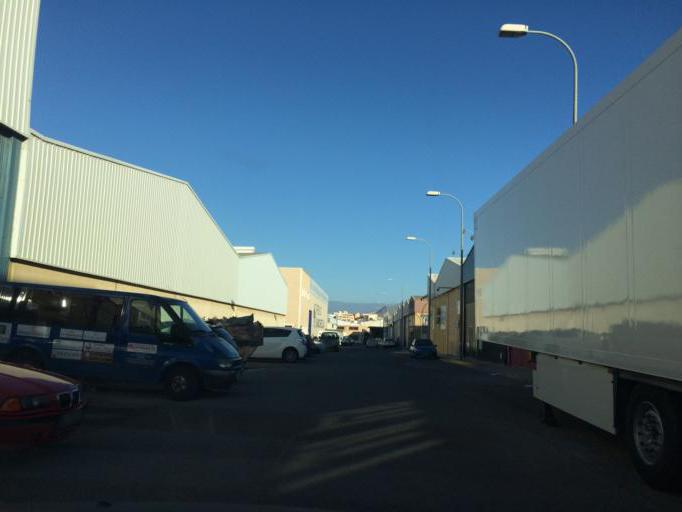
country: ES
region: Andalusia
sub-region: Provincia de Almeria
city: Viator
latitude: 36.8784
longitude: -2.4208
